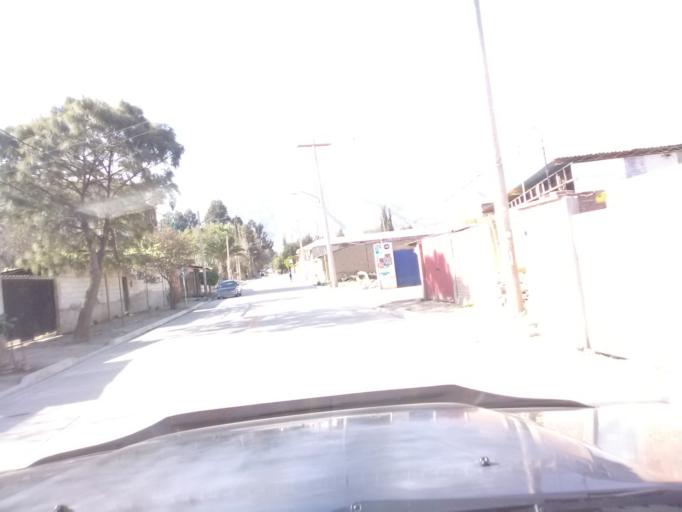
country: BO
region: Cochabamba
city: Cochabamba
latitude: -17.3602
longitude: -66.2068
